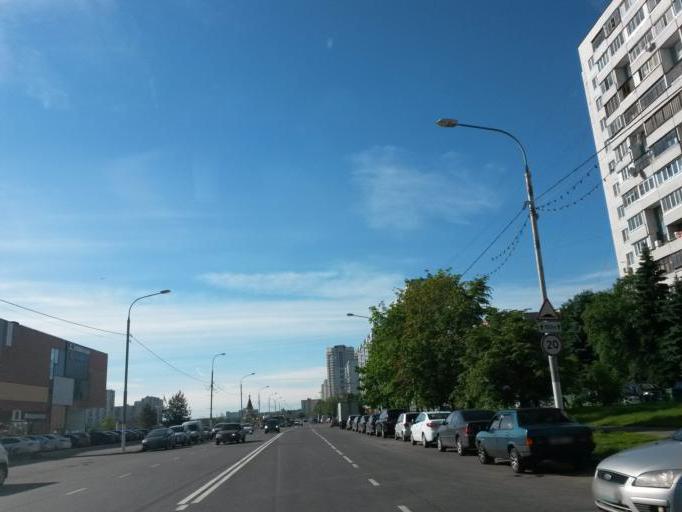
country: RU
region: Moscow
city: Brateyevo
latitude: 55.6392
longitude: 37.7573
